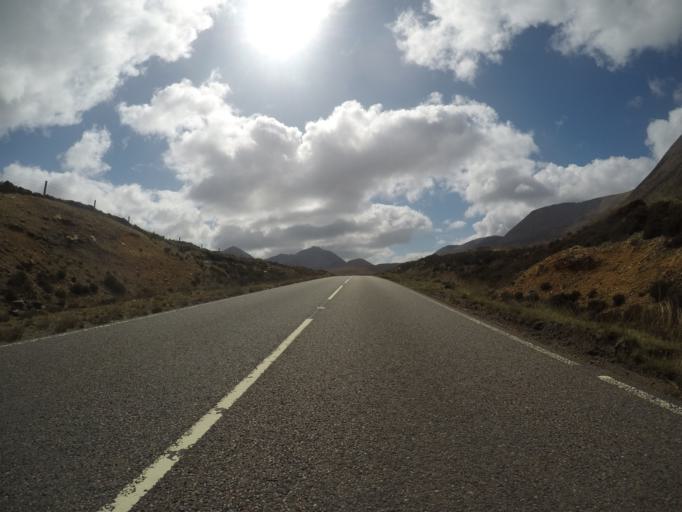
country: GB
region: Scotland
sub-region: Highland
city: Portree
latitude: 57.2813
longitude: -6.0944
